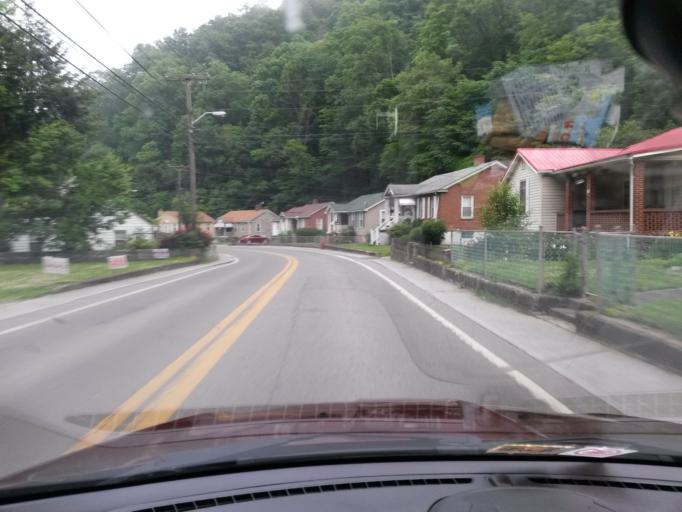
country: US
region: West Virginia
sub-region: McDowell County
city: Welch
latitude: 37.4402
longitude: -81.5841
